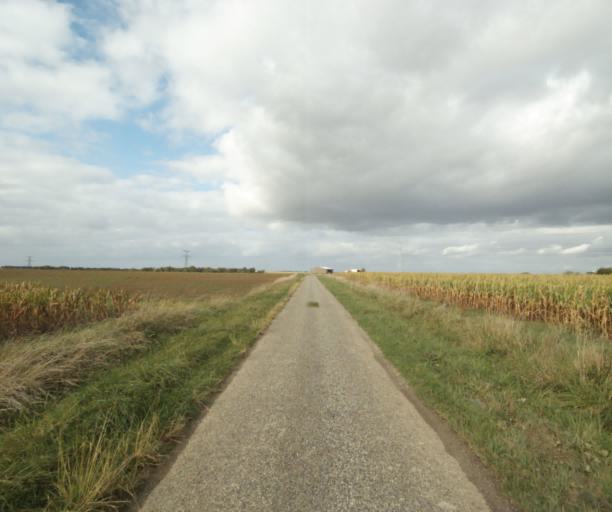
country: FR
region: Midi-Pyrenees
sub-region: Departement du Tarn-et-Garonne
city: Beaumont-de-Lomagne
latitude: 43.9018
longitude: 1.1032
